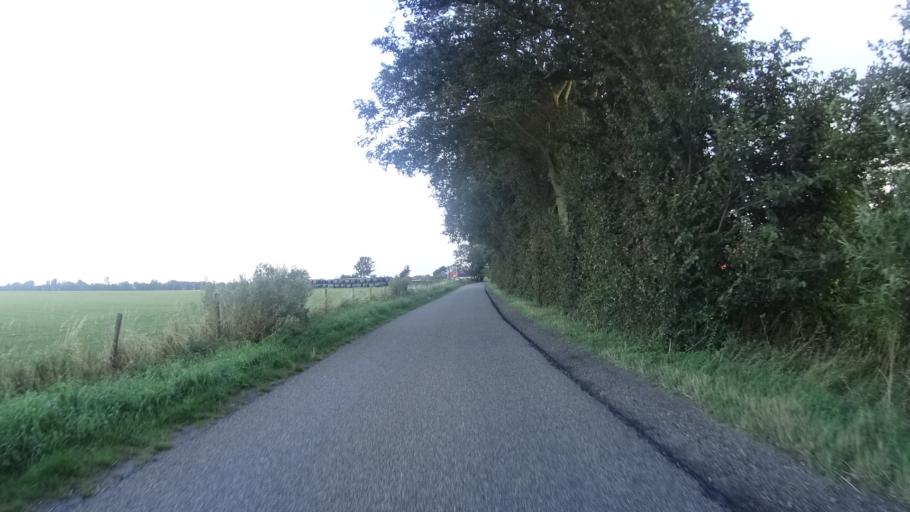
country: NL
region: North Holland
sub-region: Gemeente Hollands Kroon
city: Den Oever
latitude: 52.9261
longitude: 5.0304
